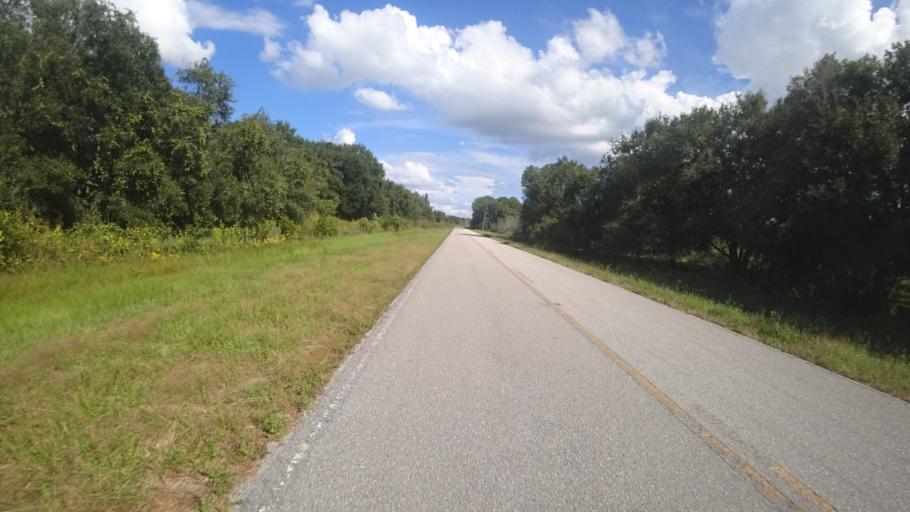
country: US
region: Florida
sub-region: DeSoto County
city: Nocatee
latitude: 27.2736
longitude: -82.1125
